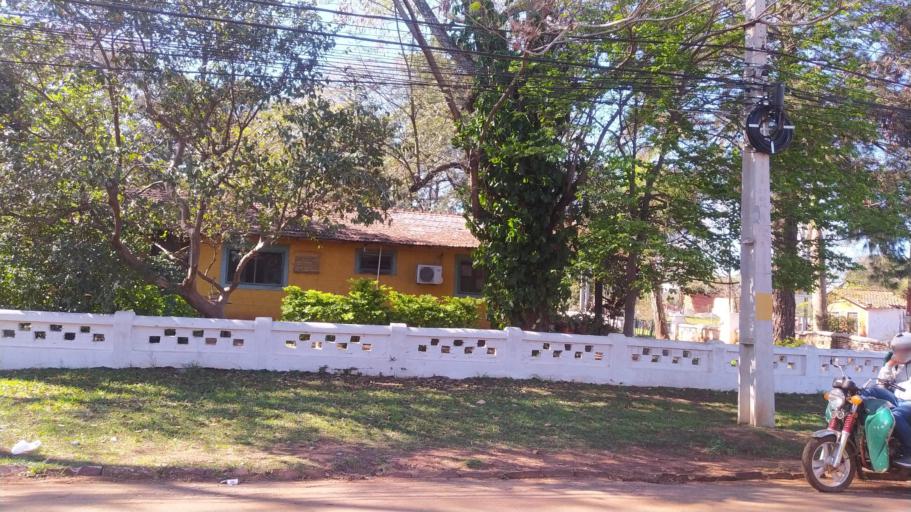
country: PY
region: Misiones
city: San Juan Bautista
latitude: -26.6703
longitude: -57.1368
